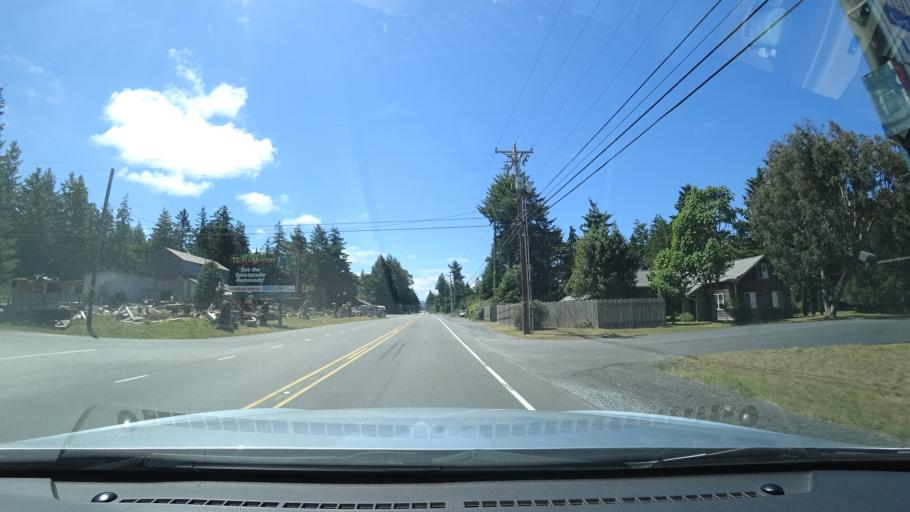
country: US
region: Oregon
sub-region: Coos County
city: Bandon
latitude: 43.0271
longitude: -124.4154
